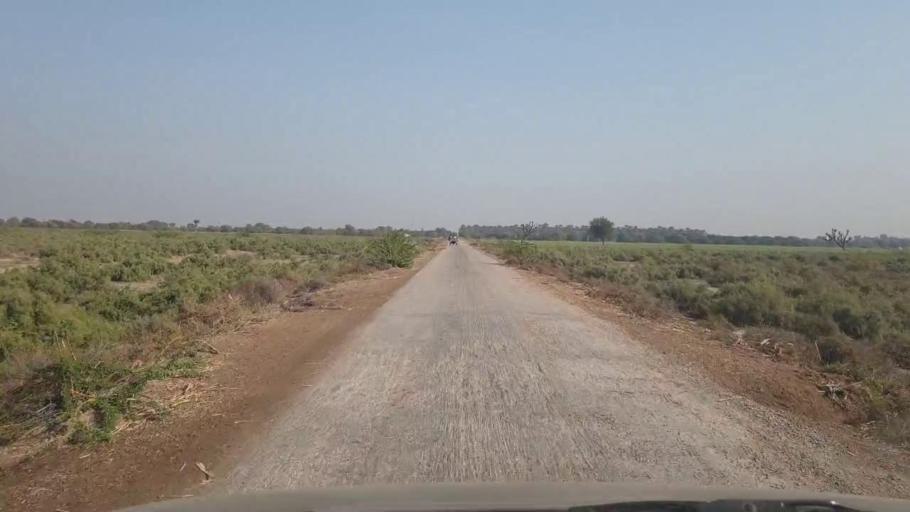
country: PK
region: Sindh
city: Digri
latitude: 25.2635
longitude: 69.1713
